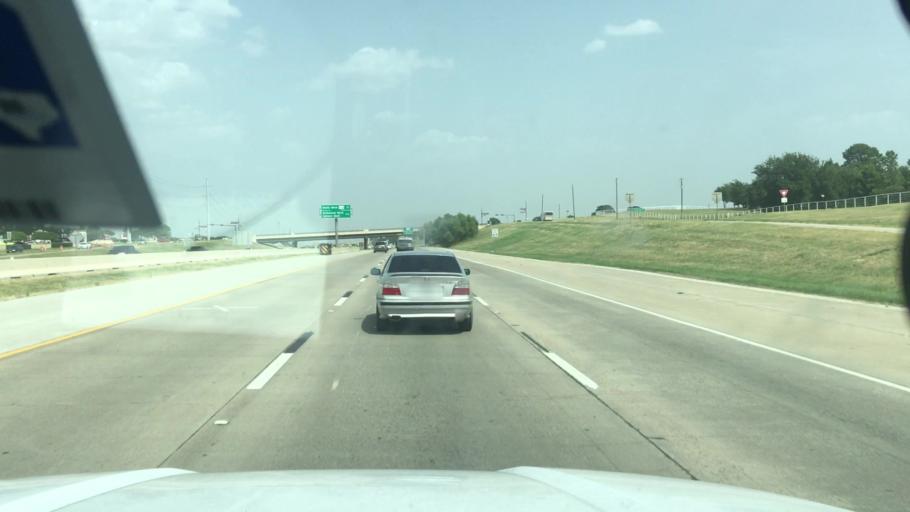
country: US
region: Texas
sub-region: Denton County
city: Trophy Club
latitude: 32.9938
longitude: -97.1964
